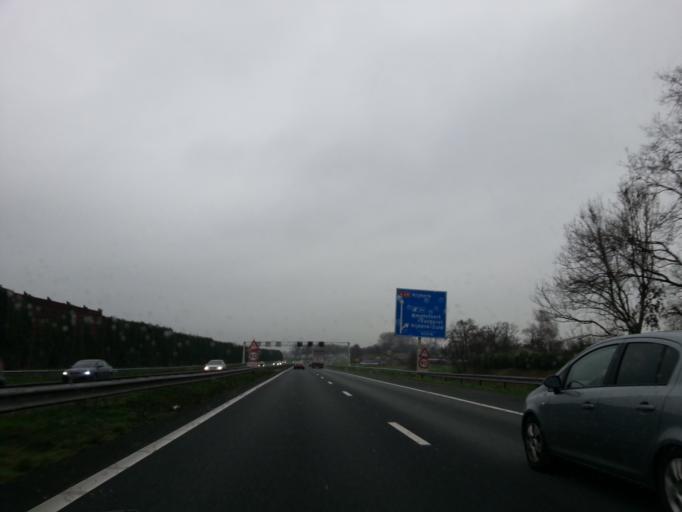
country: NL
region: Gelderland
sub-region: Gemeente Nijkerk
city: Nijkerk
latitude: 52.1980
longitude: 5.4392
